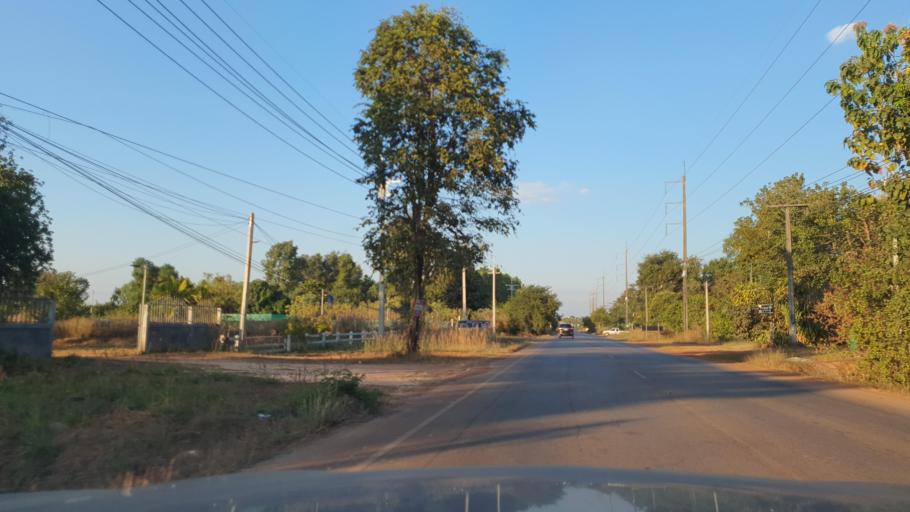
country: TH
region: Nakhon Phanom
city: Si Songkhram
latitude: 17.6024
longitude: 104.2395
